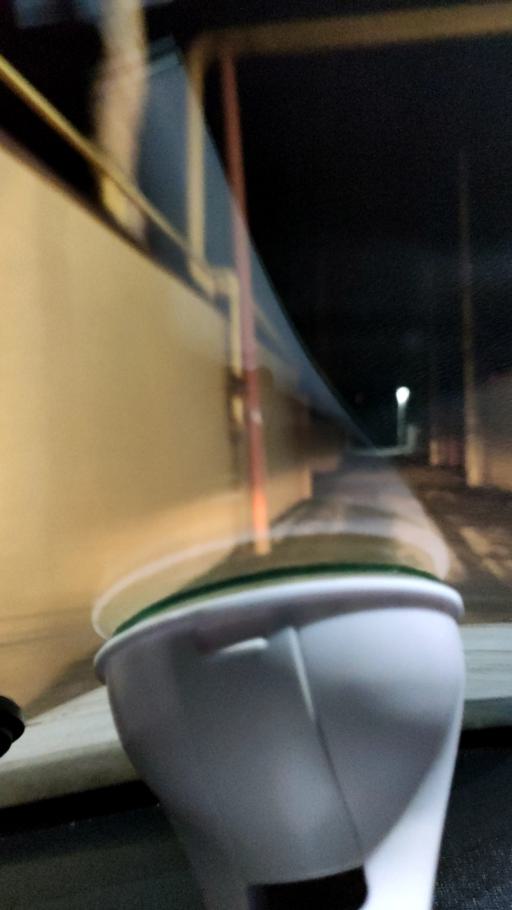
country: RU
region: Samara
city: Samara
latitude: 53.2634
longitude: 50.1920
